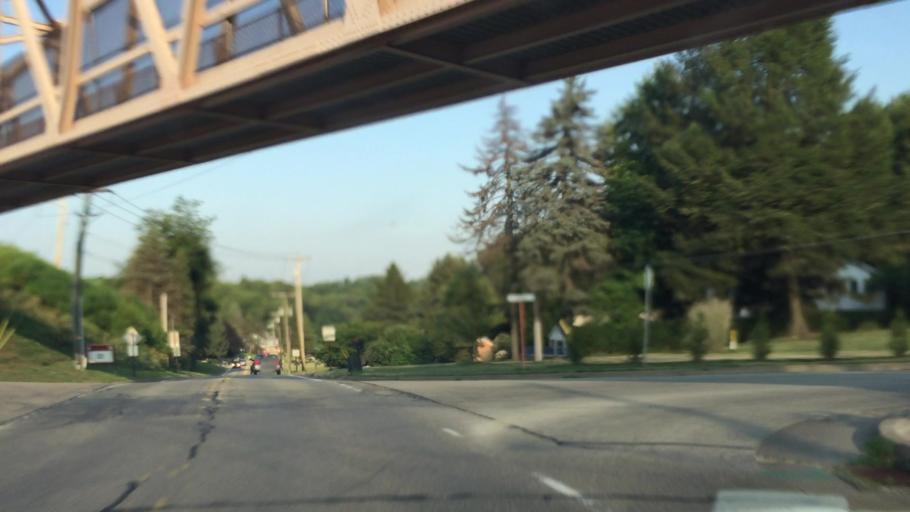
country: US
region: Pennsylvania
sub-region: Allegheny County
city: Bryn Mawr
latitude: 40.3118
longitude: -80.0651
